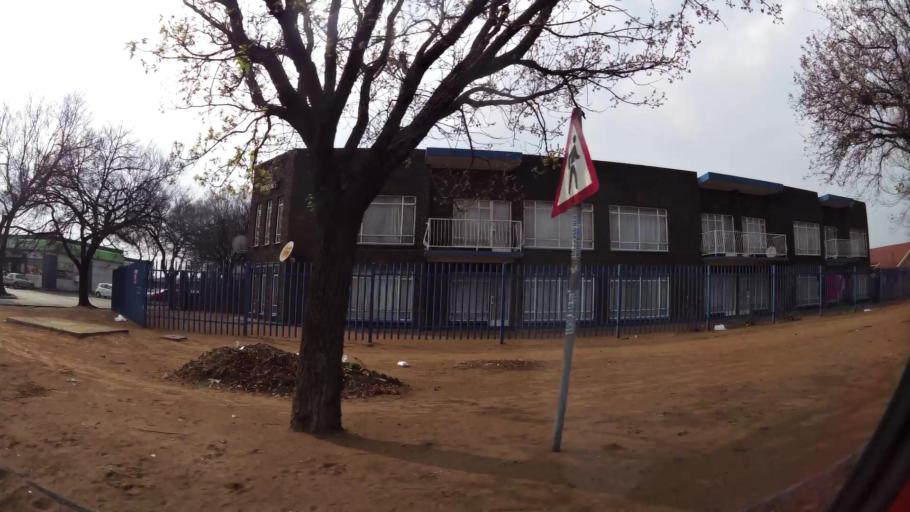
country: ZA
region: Gauteng
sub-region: Sedibeng District Municipality
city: Vanderbijlpark
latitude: -26.6851
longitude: 27.8349
